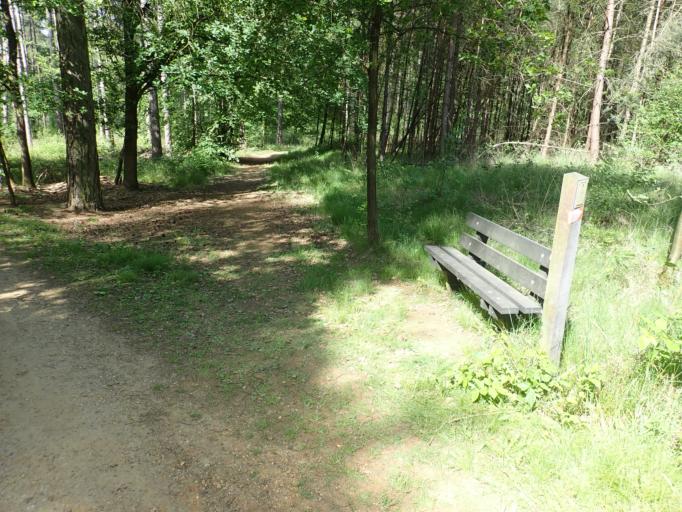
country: BE
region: Flanders
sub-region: Provincie Antwerpen
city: Westerlo
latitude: 51.0670
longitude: 4.9154
